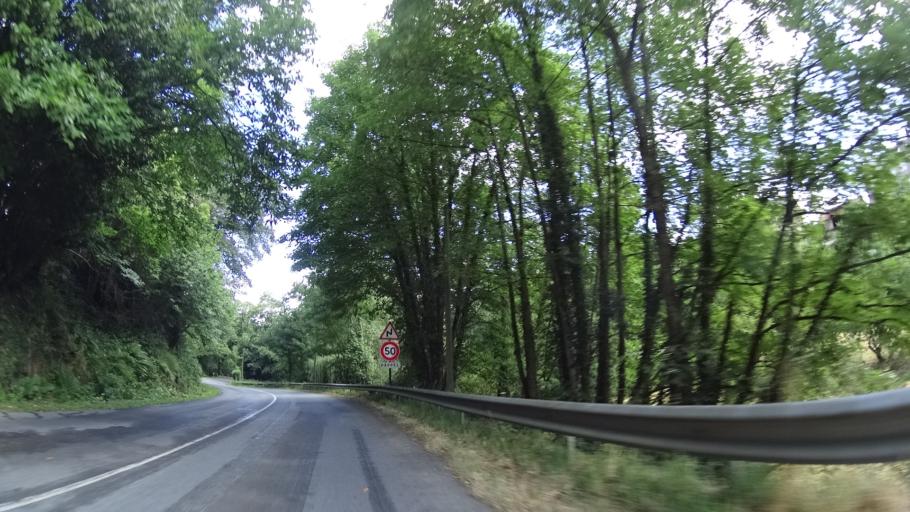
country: FR
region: Brittany
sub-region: Departement d'Ille-et-Vilaine
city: Hede-Bazouges
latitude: 48.2926
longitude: -1.8031
